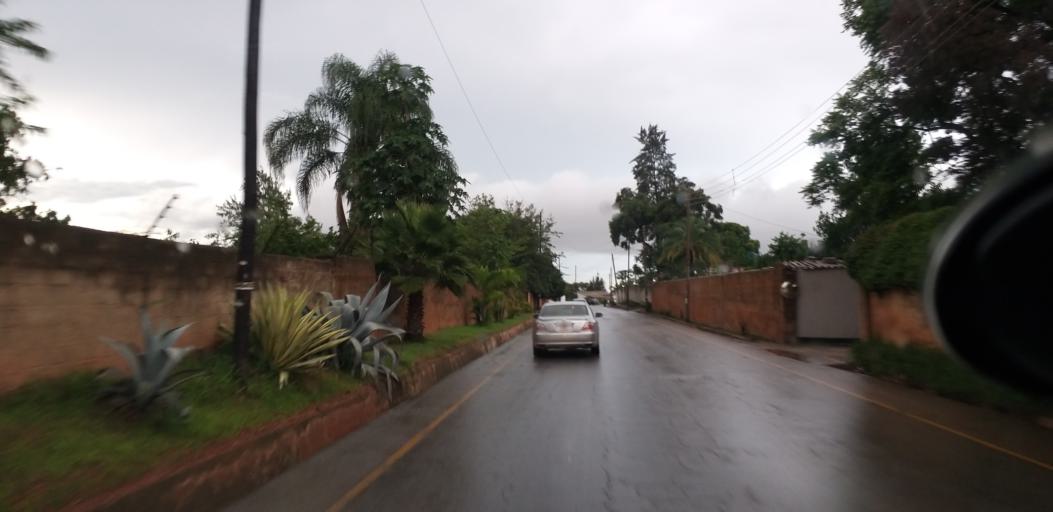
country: ZM
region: Lusaka
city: Lusaka
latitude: -15.4170
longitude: 28.3664
